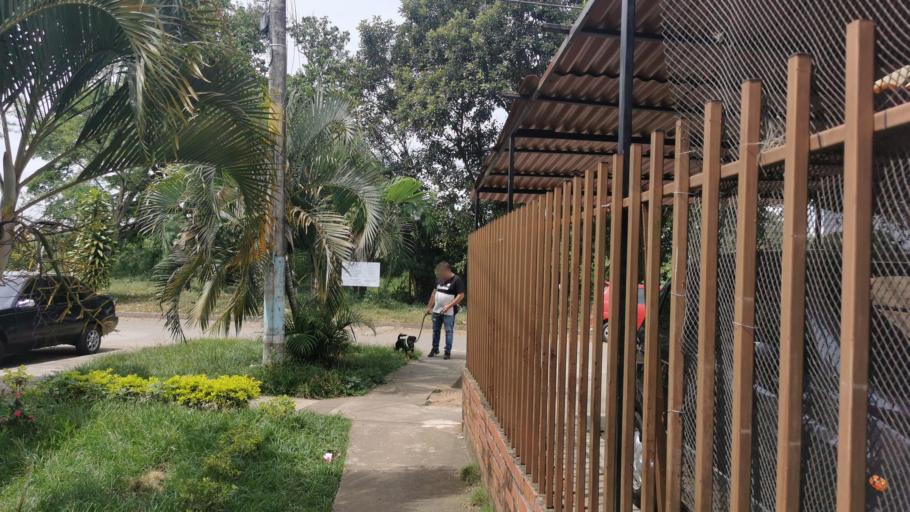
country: CO
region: Valle del Cauca
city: Jamundi
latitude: 3.2502
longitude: -76.5343
